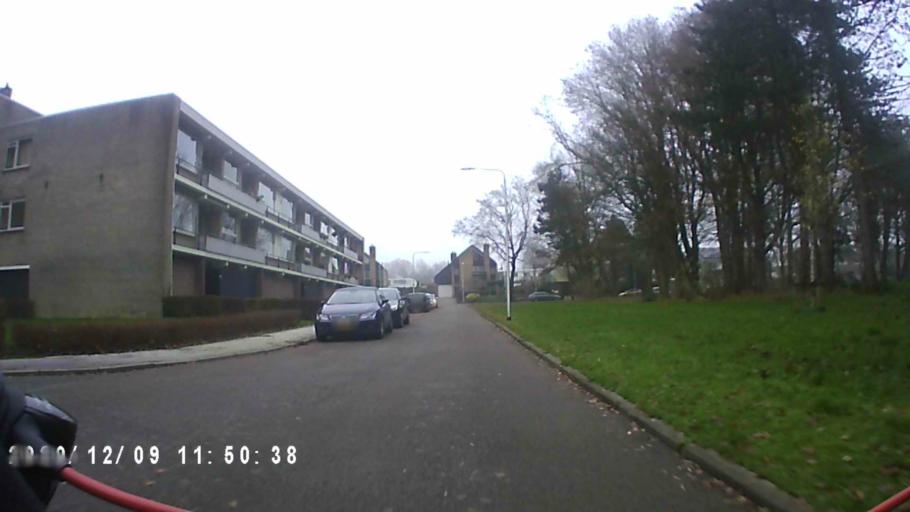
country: NL
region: Groningen
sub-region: Gemeente Haren
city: Haren
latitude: 53.1739
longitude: 6.5988
